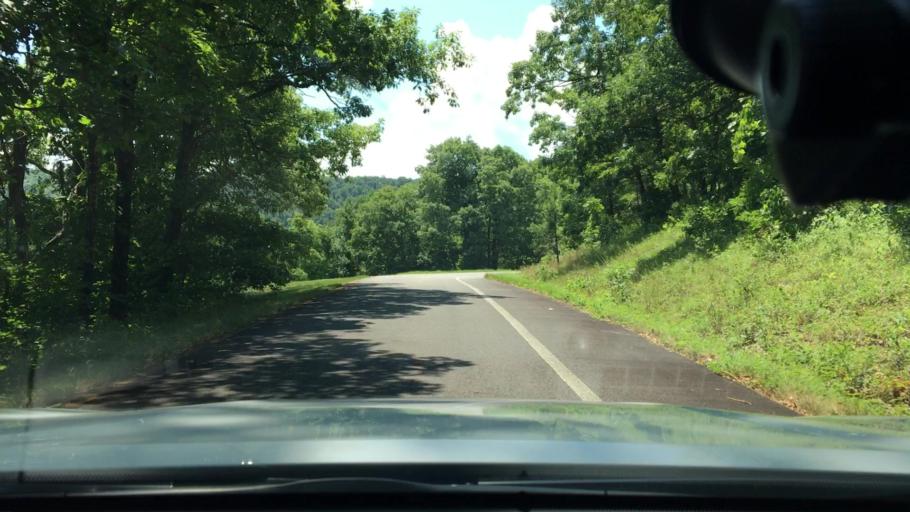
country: US
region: Arkansas
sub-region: Logan County
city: Paris
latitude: 35.1731
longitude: -93.6409
